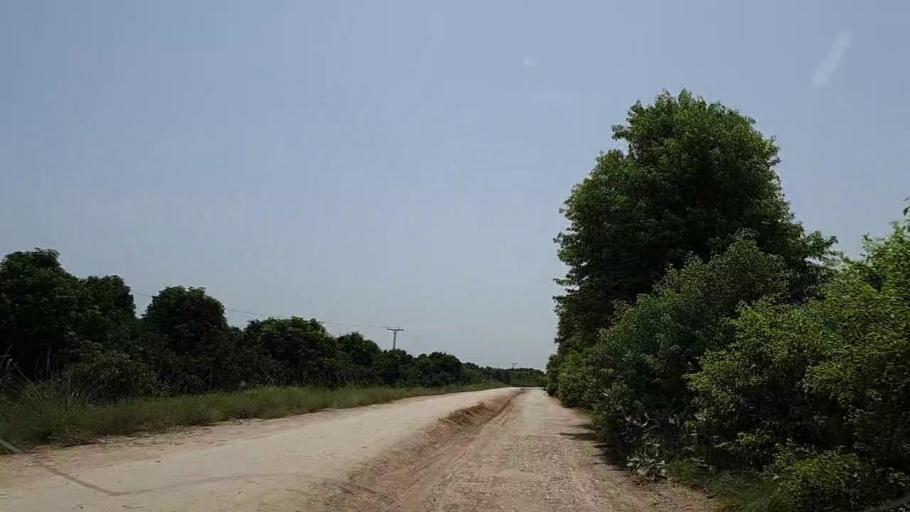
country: PK
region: Sindh
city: Tharu Shah
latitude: 27.0000
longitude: 68.1187
